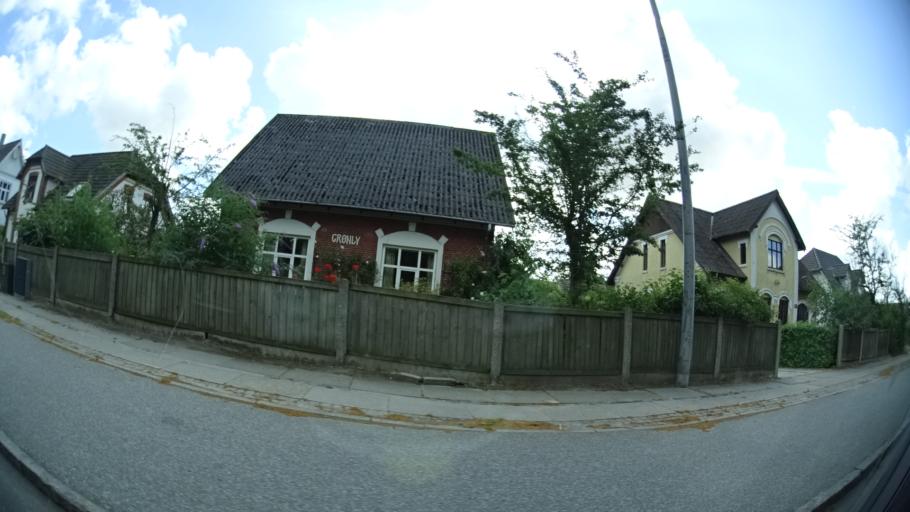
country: DK
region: Central Jutland
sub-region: Odder Kommune
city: Odder
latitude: 55.9773
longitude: 10.1507
